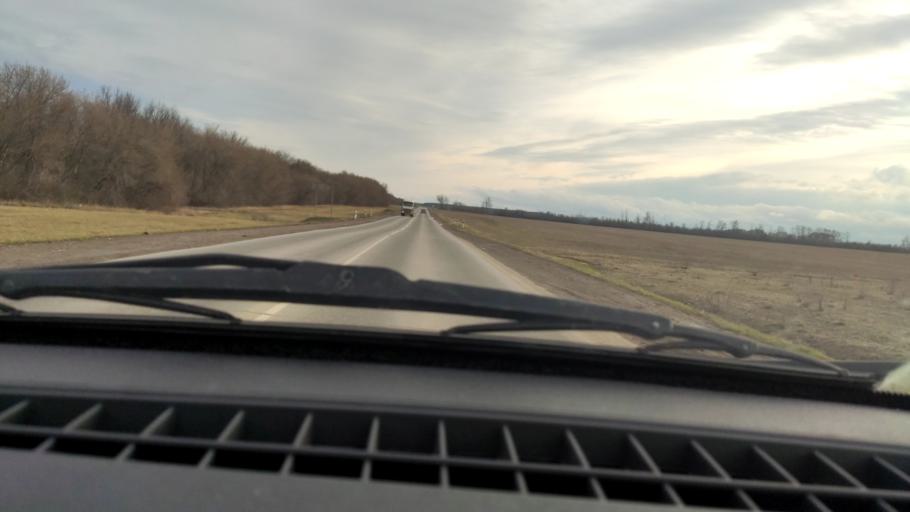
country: RU
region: Bashkortostan
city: Davlekanovo
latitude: 54.2746
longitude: 55.1027
